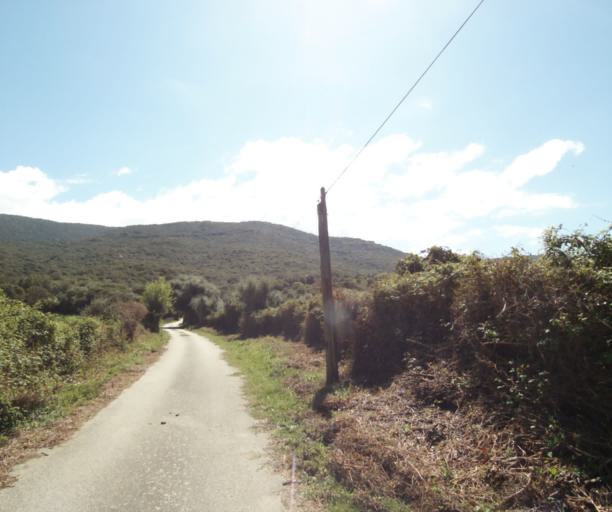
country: FR
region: Corsica
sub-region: Departement de la Corse-du-Sud
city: Propriano
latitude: 41.6428
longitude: 8.8697
